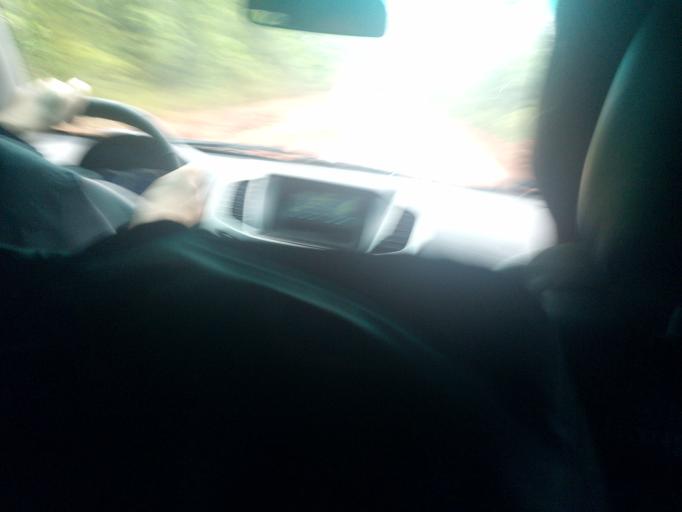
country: LA
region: Bolikhamxai
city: Bolikhan
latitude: 18.5519
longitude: 103.7817
